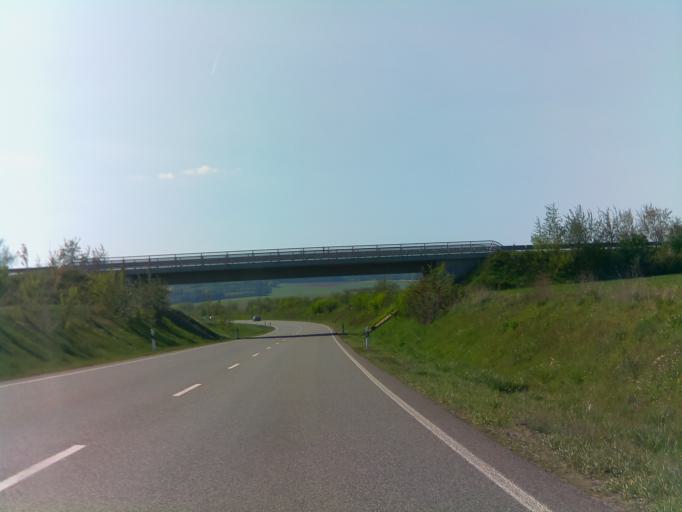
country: DE
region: Thuringia
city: Miesitz
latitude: 50.7378
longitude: 11.8242
